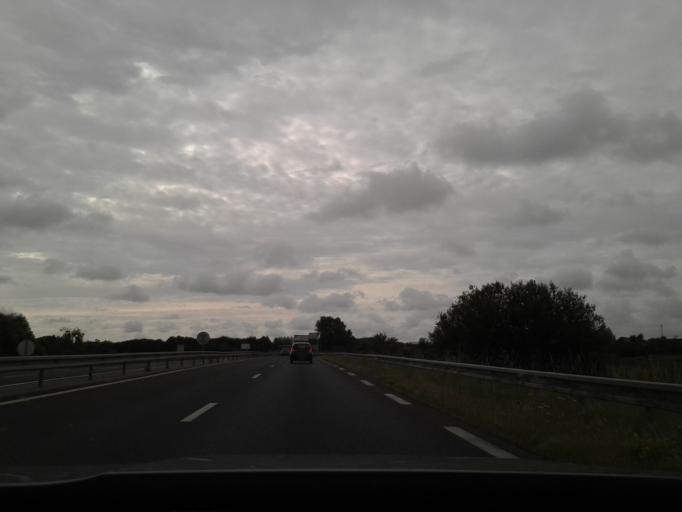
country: FR
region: Lower Normandy
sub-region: Departement de la Manche
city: Saint-Hilaire-Petitville
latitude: 49.3123
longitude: -1.2264
